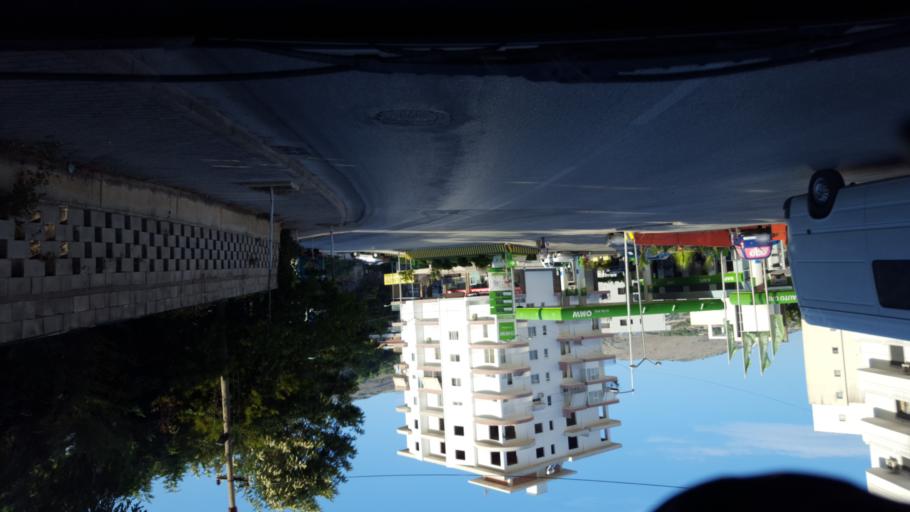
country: AL
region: Vlore
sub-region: Rrethi i Sarandes
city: Sarande
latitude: 39.8691
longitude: 20.0194
